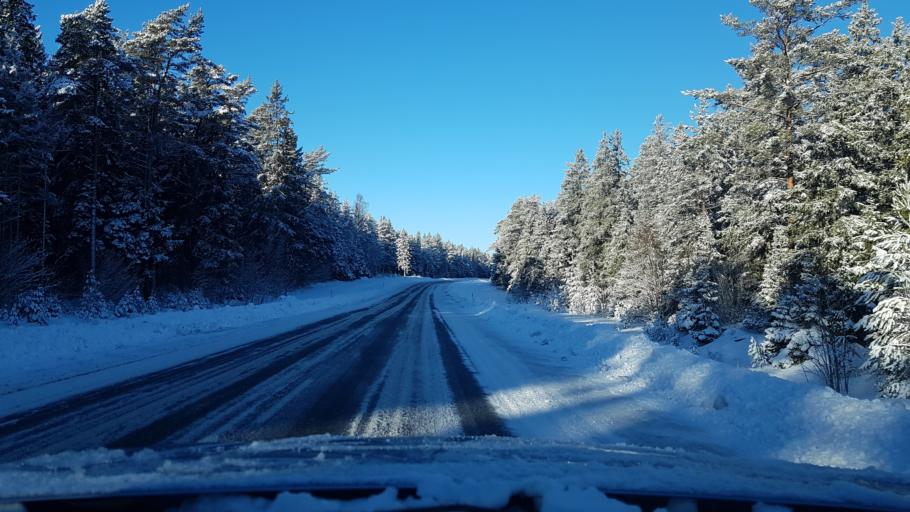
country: EE
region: Hiiumaa
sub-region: Kaerdla linn
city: Kardla
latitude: 58.9643
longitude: 22.8387
